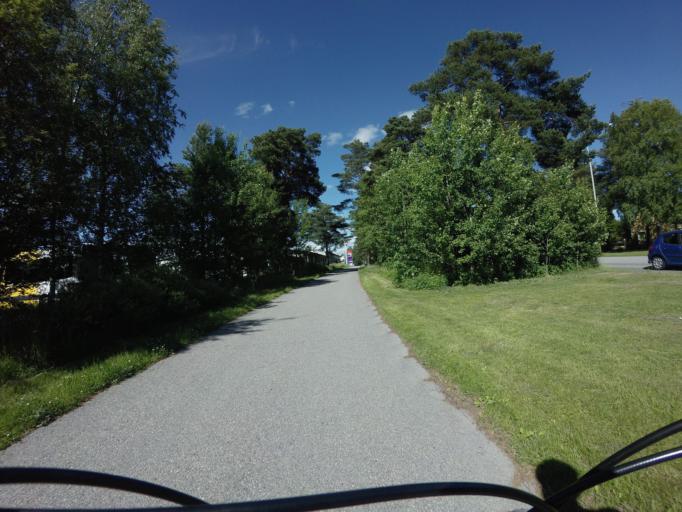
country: FI
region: Varsinais-Suomi
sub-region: Turku
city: Turku
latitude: 60.4817
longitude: 22.2714
